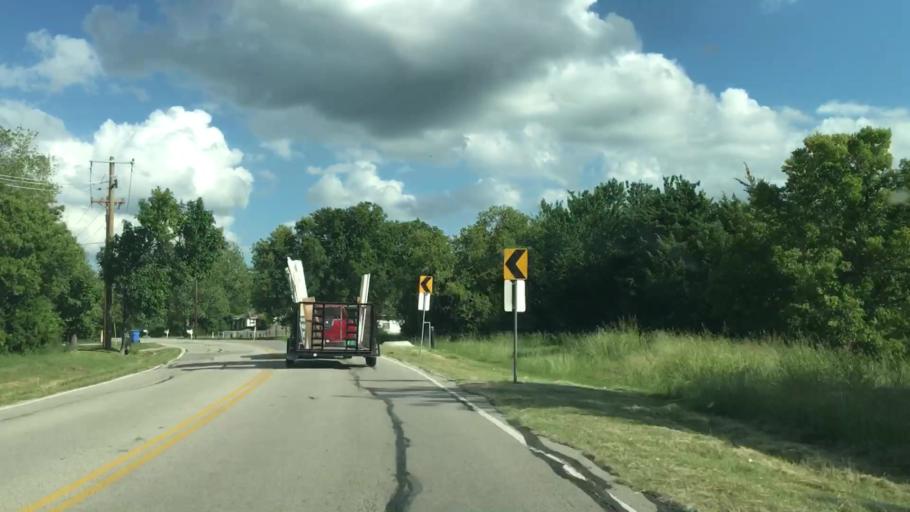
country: US
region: Texas
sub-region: Dallas County
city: Rowlett
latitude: 32.8811
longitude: -96.5233
